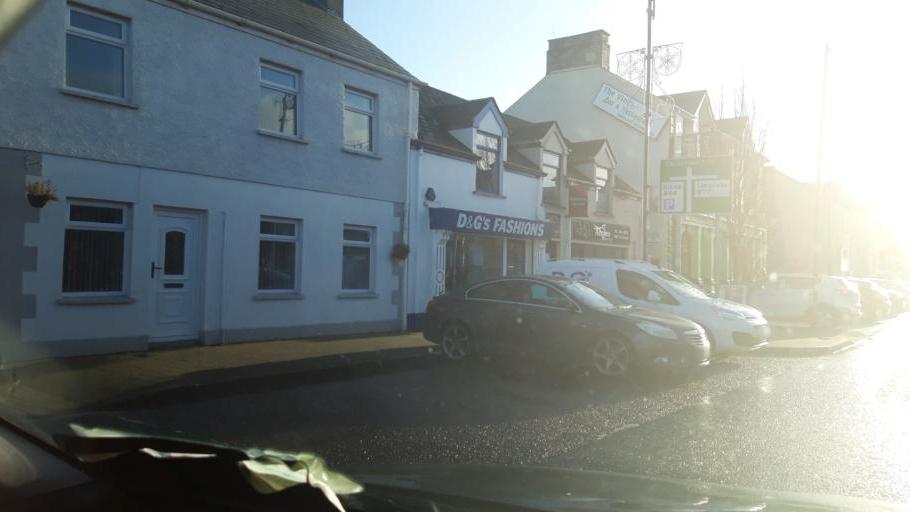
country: GB
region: Northern Ireland
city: Garvagh
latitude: 54.9841
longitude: -6.6872
